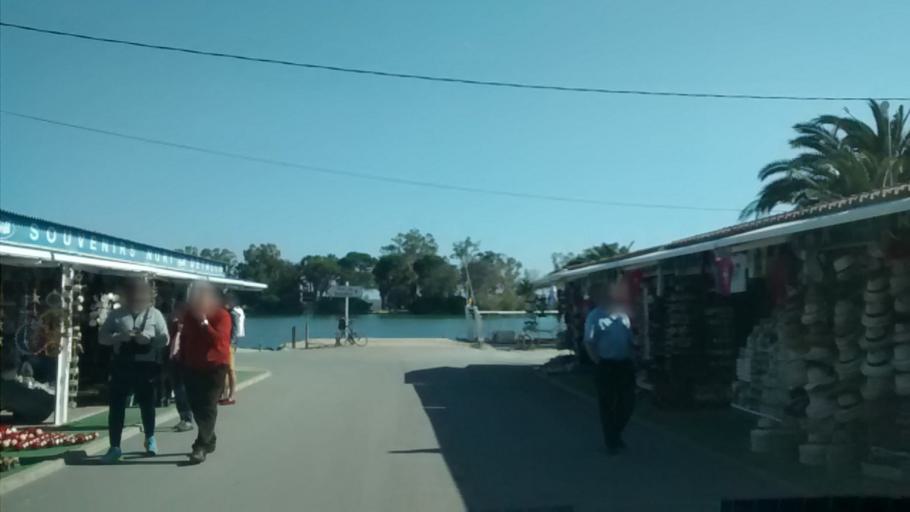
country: ES
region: Catalonia
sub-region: Provincia de Tarragona
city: Deltebre
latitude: 40.7133
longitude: 0.8345
